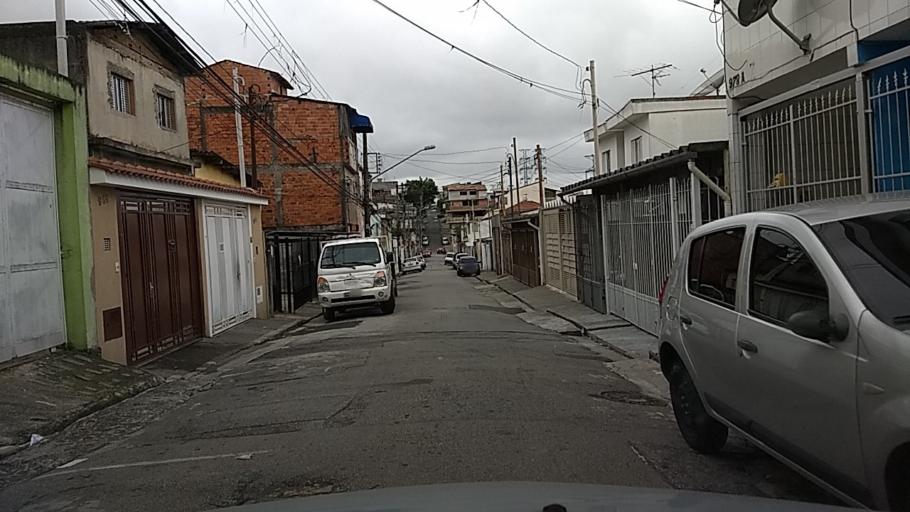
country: BR
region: Sao Paulo
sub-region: Guarulhos
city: Guarulhos
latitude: -23.4935
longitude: -46.5852
